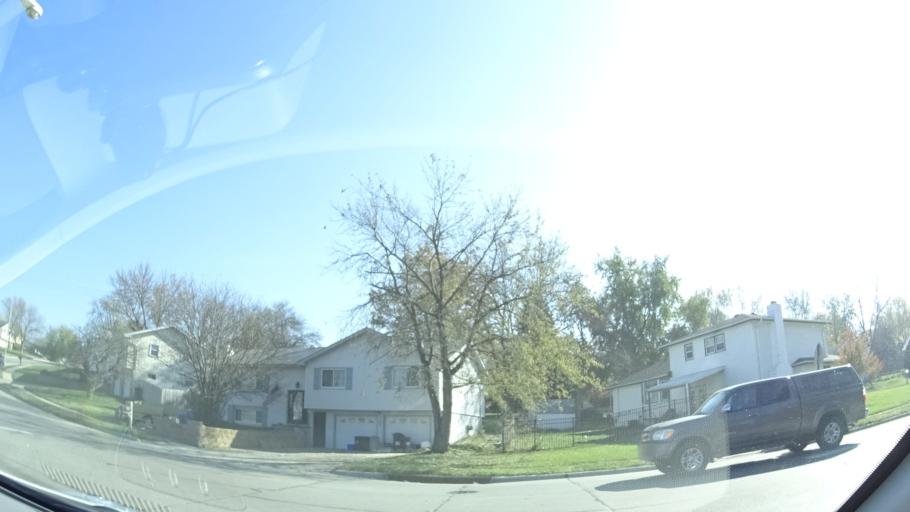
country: US
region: Nebraska
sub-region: Sarpy County
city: Offutt Air Force Base
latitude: 41.1354
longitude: -95.9631
